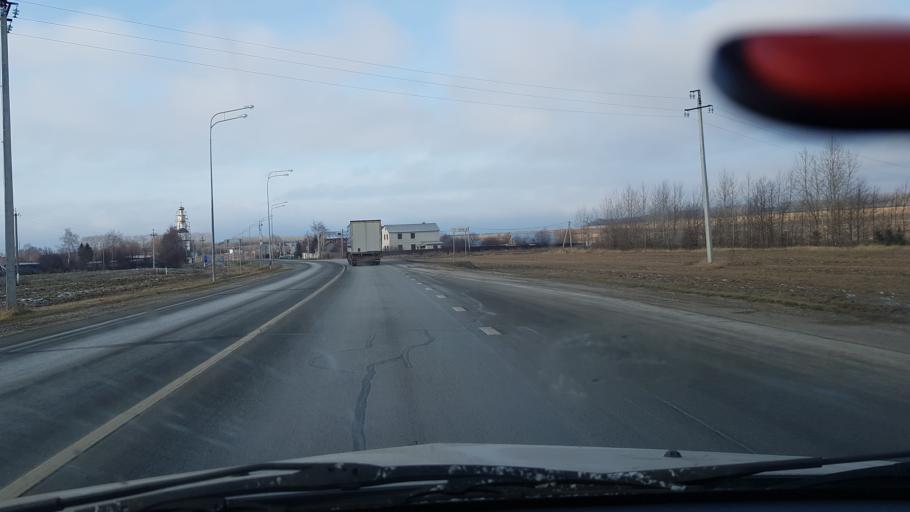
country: RU
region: Tatarstan
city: Laishevo
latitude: 55.3916
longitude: 49.8068
